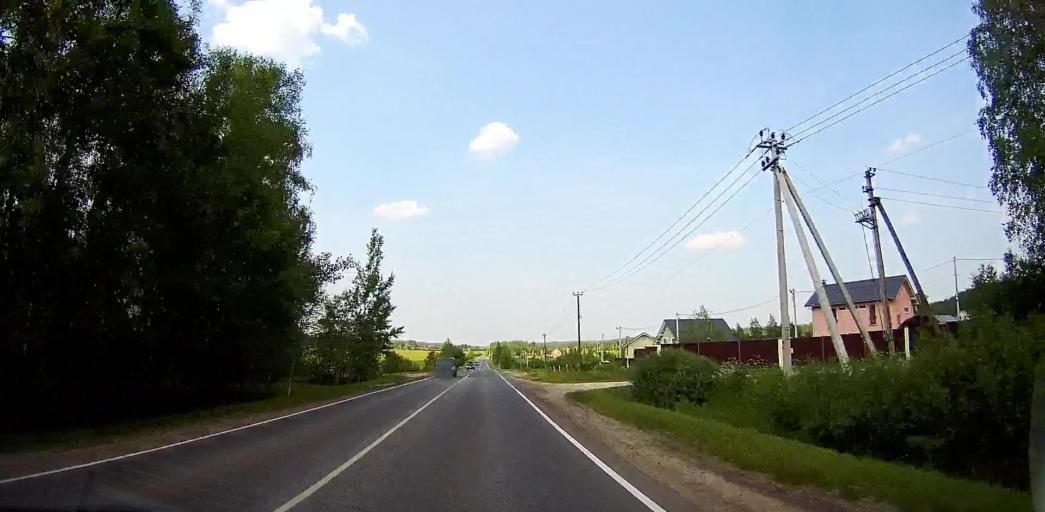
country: RU
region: Moskovskaya
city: Mikhnevo
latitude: 55.1715
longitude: 37.9634
